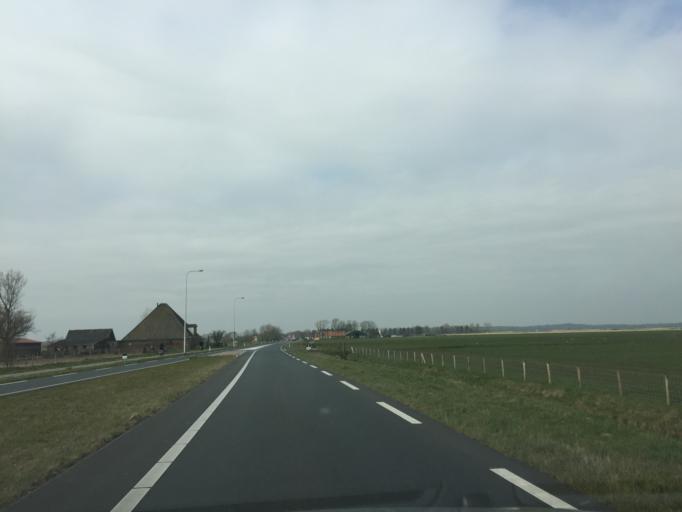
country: NL
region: North Holland
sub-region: Gemeente Alkmaar
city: Alkmaar
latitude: 52.6365
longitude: 4.7094
